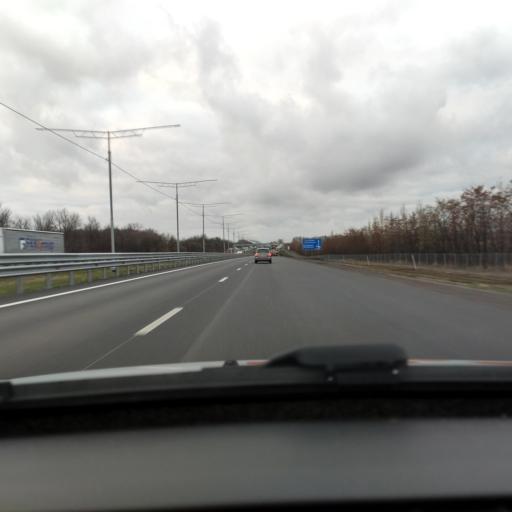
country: RU
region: Voronezj
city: Ramon'
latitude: 52.0010
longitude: 39.2169
